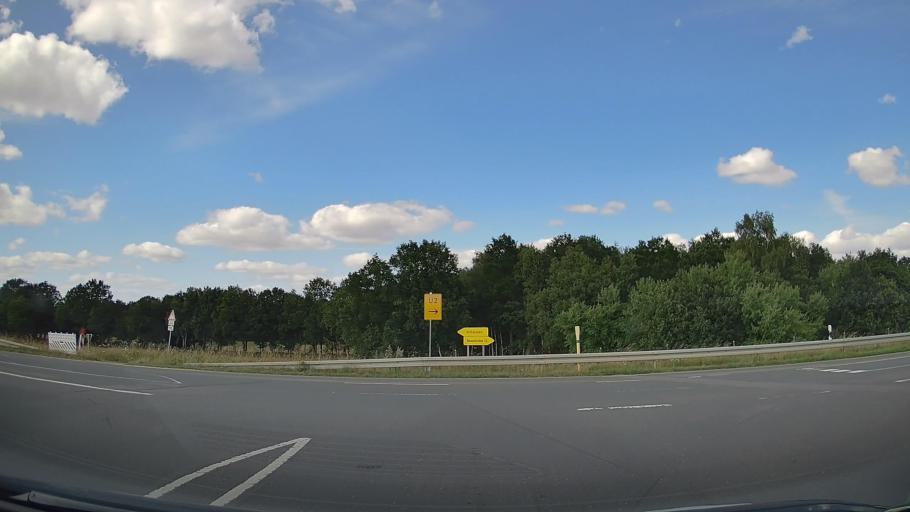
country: DE
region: Lower Saxony
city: Rieste
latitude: 52.4943
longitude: 7.9868
